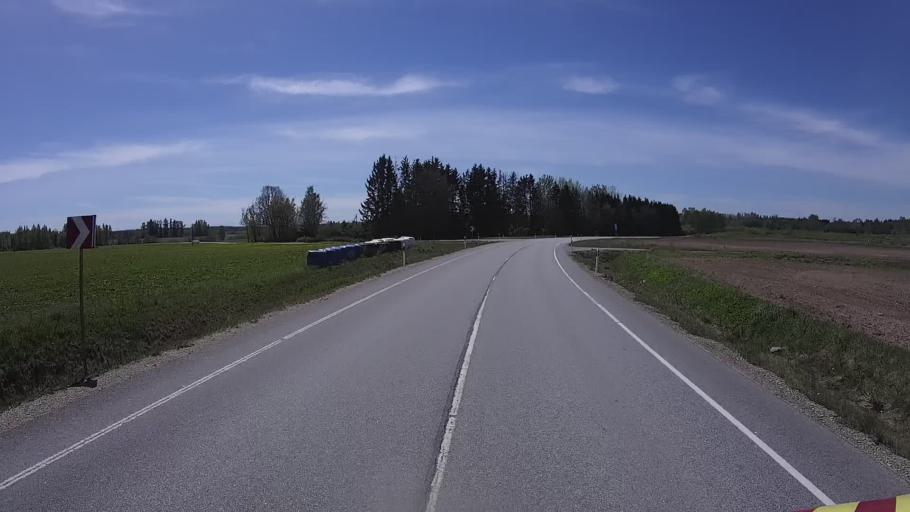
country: EE
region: Vorumaa
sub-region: Voru linn
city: Voru
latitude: 57.8918
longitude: 27.1784
